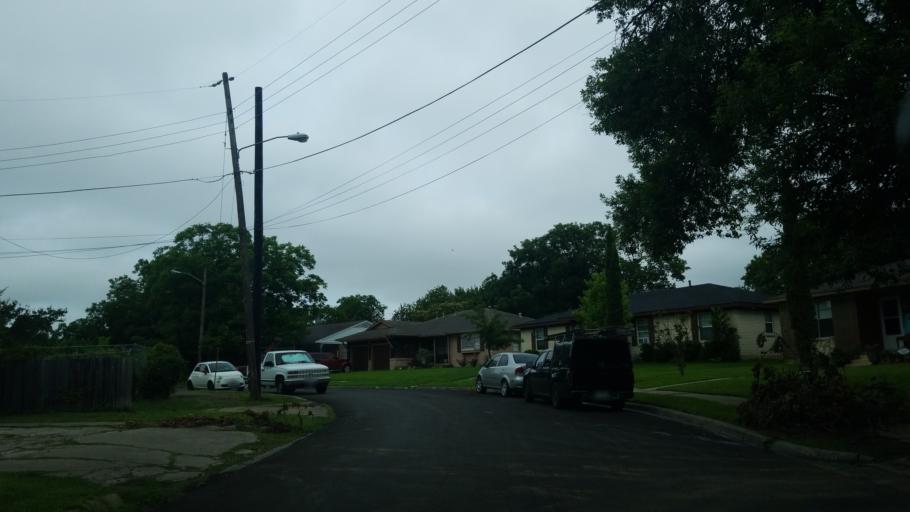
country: US
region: Texas
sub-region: Dallas County
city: Farmers Branch
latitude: 32.8940
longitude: -96.8783
